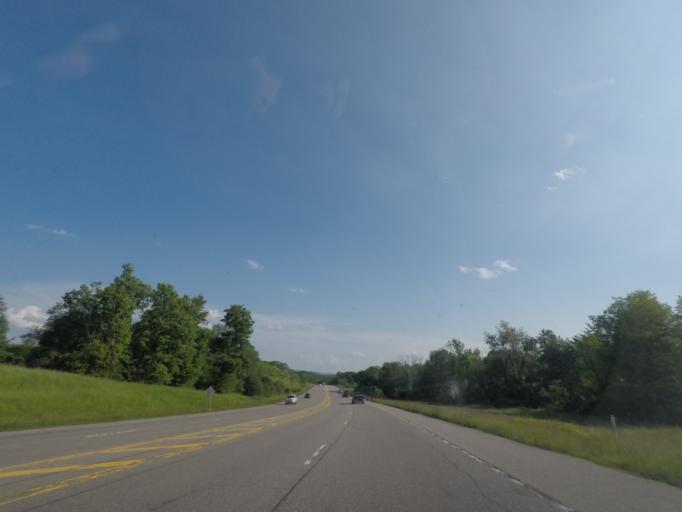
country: US
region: New York
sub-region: Orange County
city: Orange Lake
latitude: 41.5038
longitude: -74.1351
